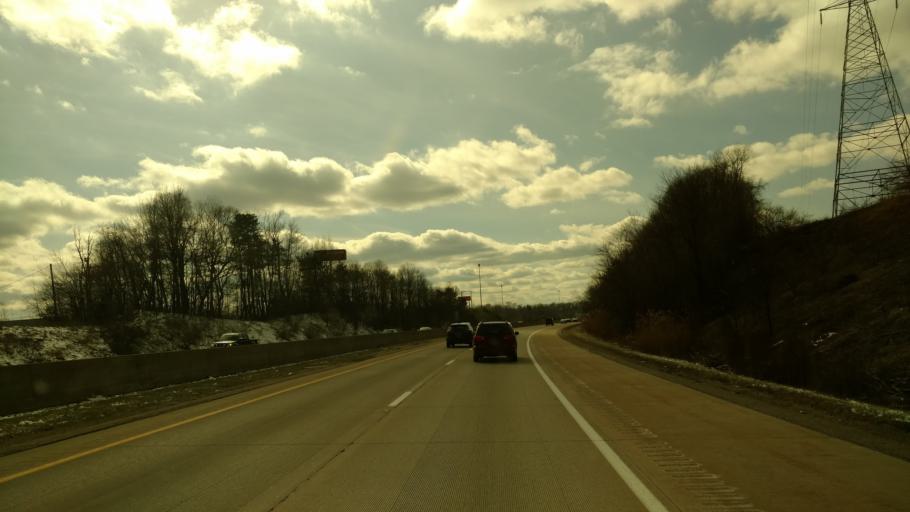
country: US
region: Ohio
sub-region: Summit County
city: Sawyerwood
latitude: 41.0667
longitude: -81.4272
